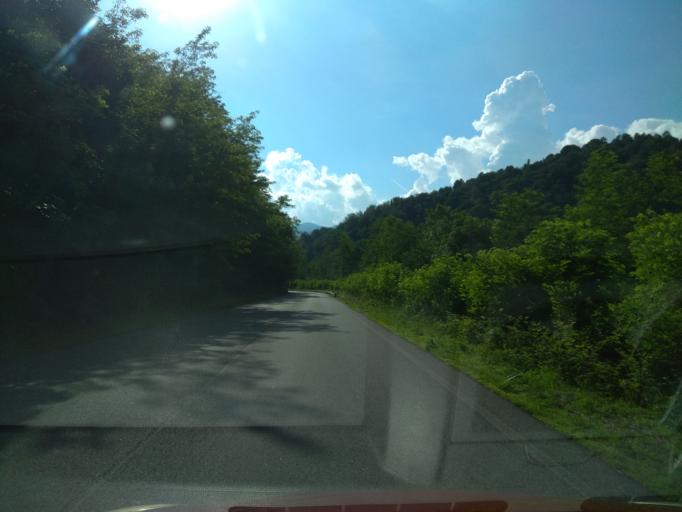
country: IT
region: Piedmont
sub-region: Provincia di Biella
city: Pray
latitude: 45.6741
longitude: 8.2280
